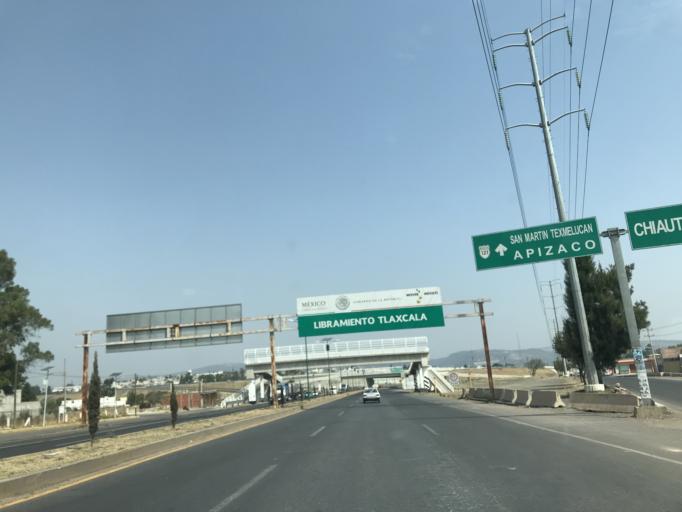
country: MX
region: Tlaxcala
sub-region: Chiautempan
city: Santa Cruz Tetela
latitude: 19.3012
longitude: -98.1970
